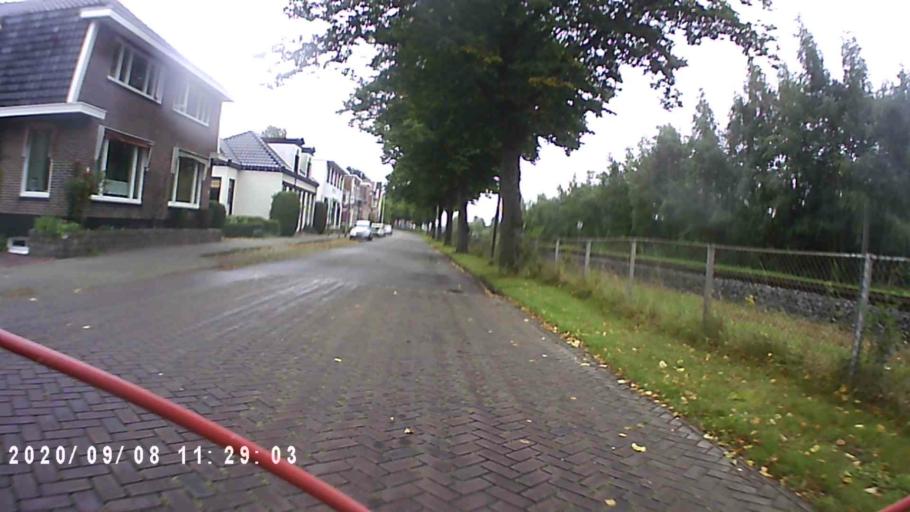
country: NL
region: Groningen
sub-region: Gemeente Hoogezand-Sappemeer
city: Hoogezand
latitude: 53.1600
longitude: 6.7671
